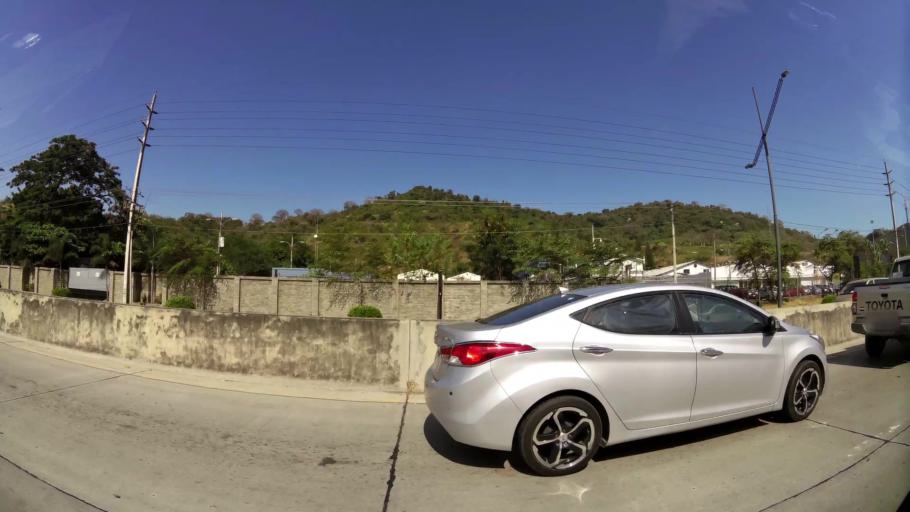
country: EC
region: Guayas
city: Guayaquil
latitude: -2.1717
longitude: -79.9392
